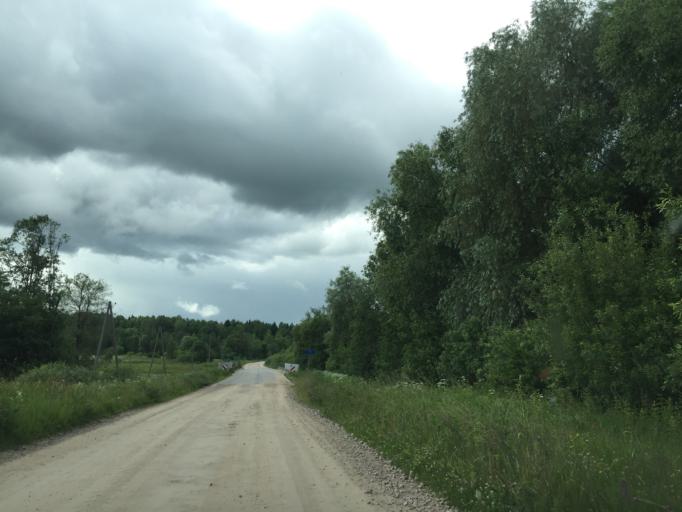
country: LV
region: Lecava
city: Iecava
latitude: 56.6237
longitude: 24.1846
